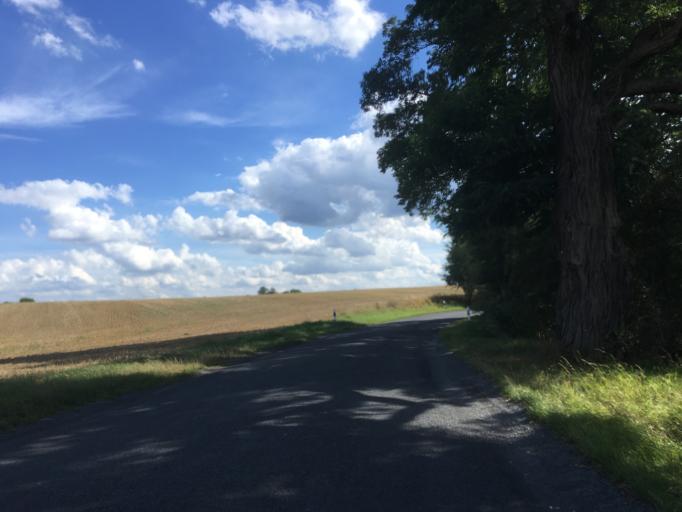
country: DE
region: Brandenburg
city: Angermunde
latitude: 52.9569
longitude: 14.0029
